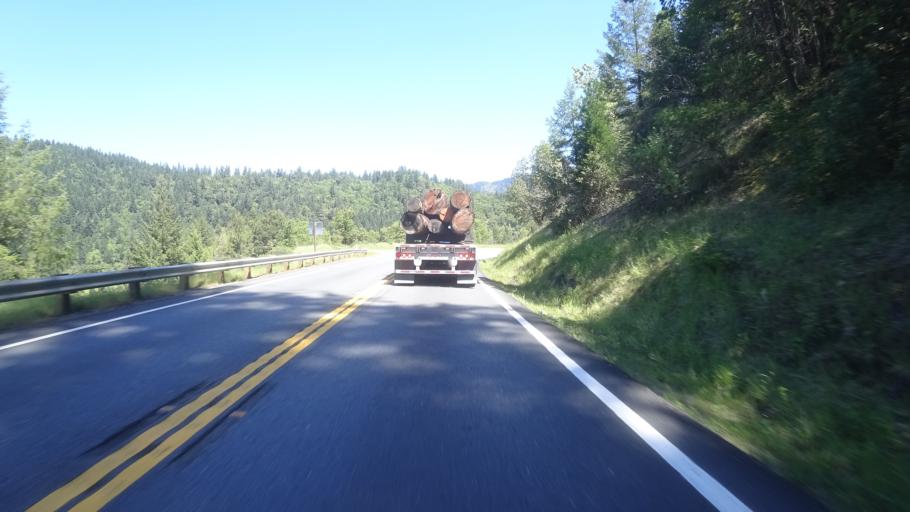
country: US
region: California
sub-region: Humboldt County
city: Willow Creek
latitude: 40.9460
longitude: -123.6527
